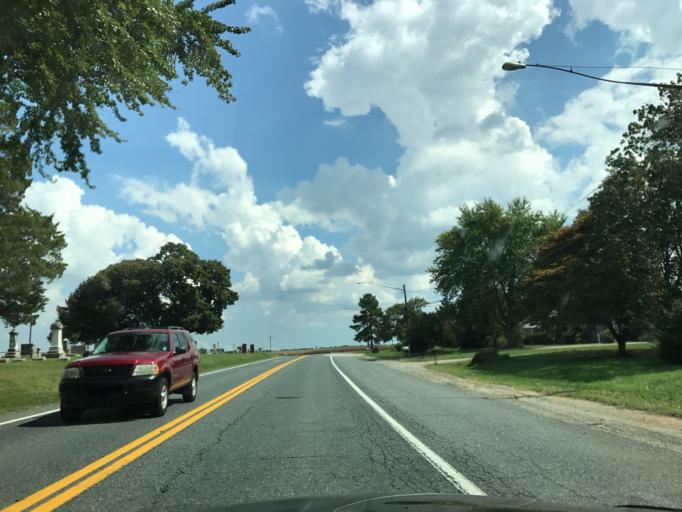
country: US
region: Maryland
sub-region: Queen Anne's County
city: Kingstown
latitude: 39.1885
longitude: -75.8508
